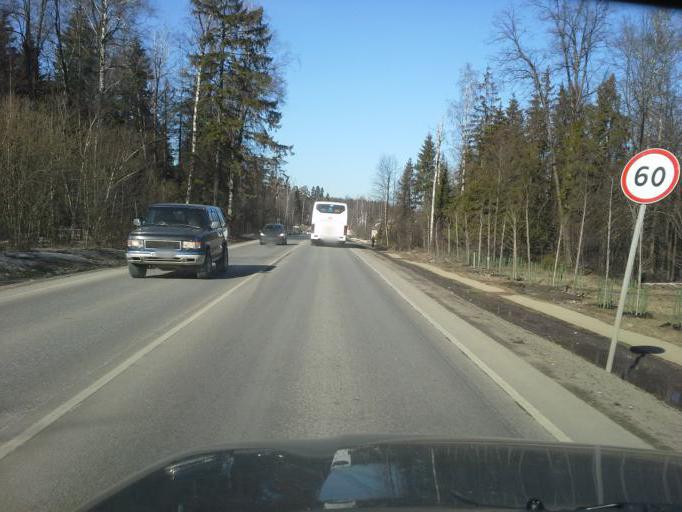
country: RU
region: Moskovskaya
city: Lesnoy Gorodok
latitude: 55.6653
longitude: 37.1782
